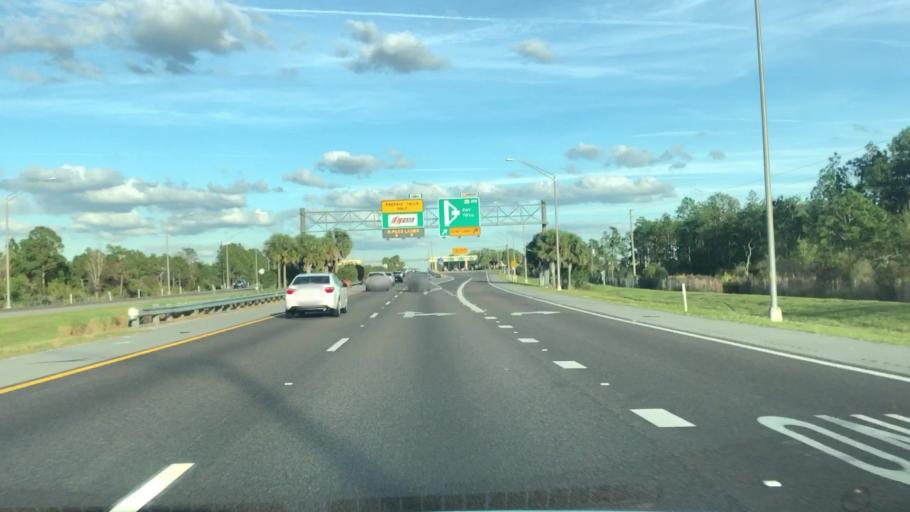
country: US
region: Florida
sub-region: Orange County
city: Hunters Creek
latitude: 28.3544
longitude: -81.4641
